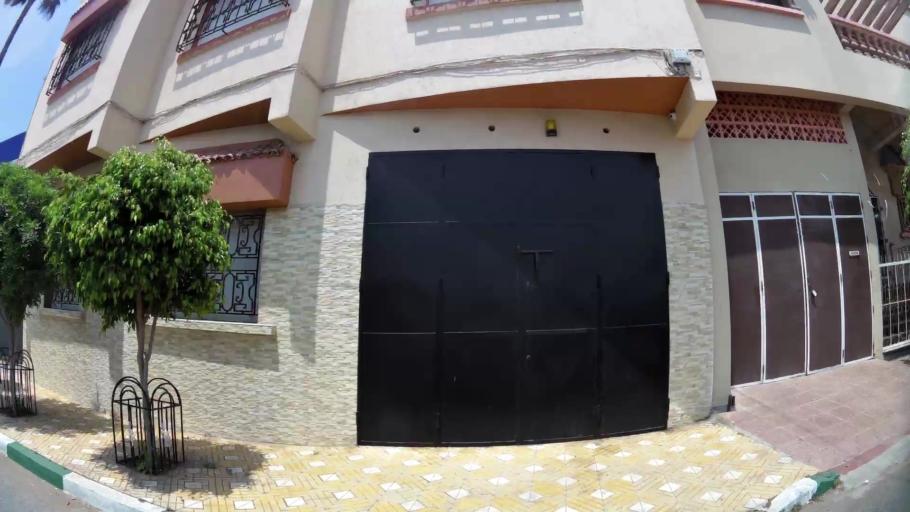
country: MA
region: Rabat-Sale-Zemmour-Zaer
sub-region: Skhirate-Temara
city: Temara
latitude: 33.9788
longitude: -6.8914
